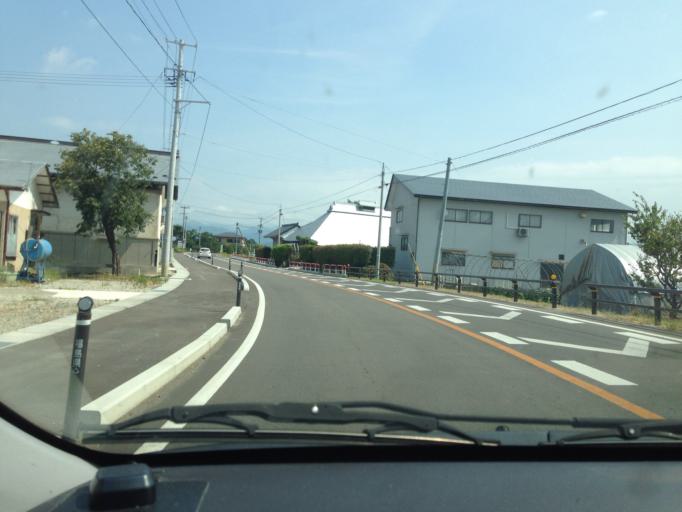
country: JP
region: Fukushima
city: Kitakata
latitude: 37.6186
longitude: 139.8634
